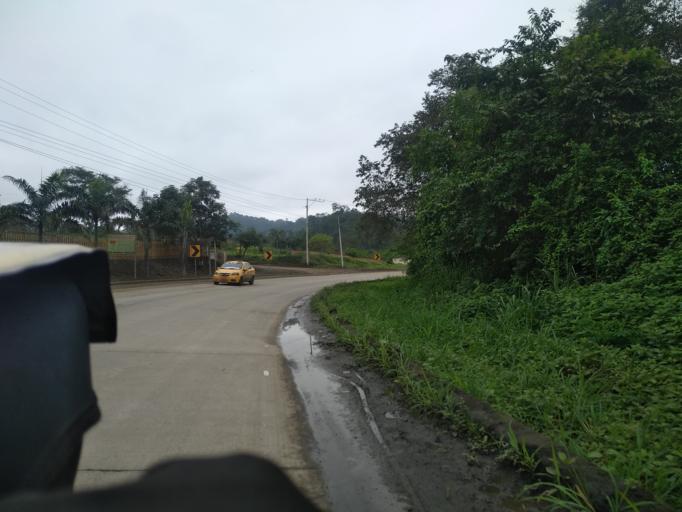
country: EC
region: Manabi
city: Jipijapa
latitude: -1.6703
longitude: -80.8082
